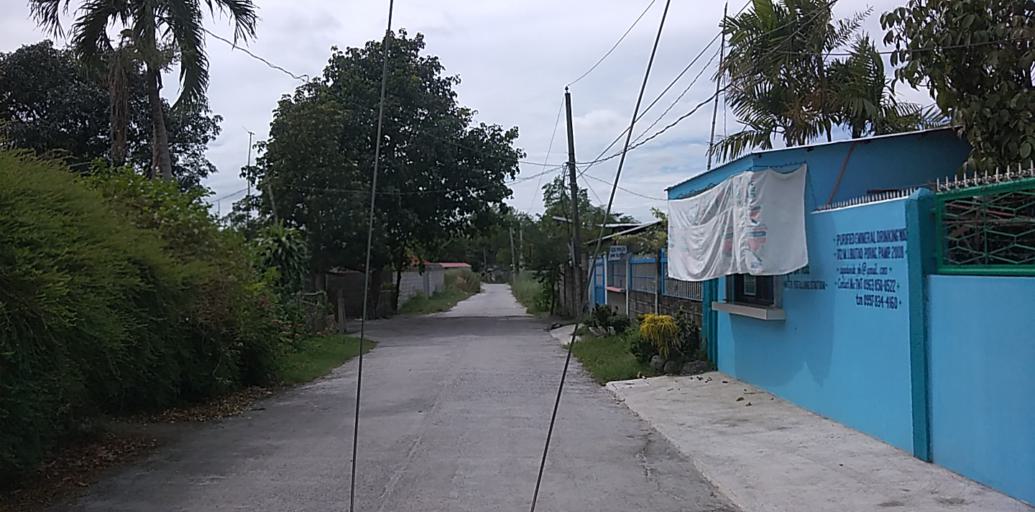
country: PH
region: Central Luzon
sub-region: Province of Pampanga
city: Manibaug Pasig
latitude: 15.1085
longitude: 120.5597
